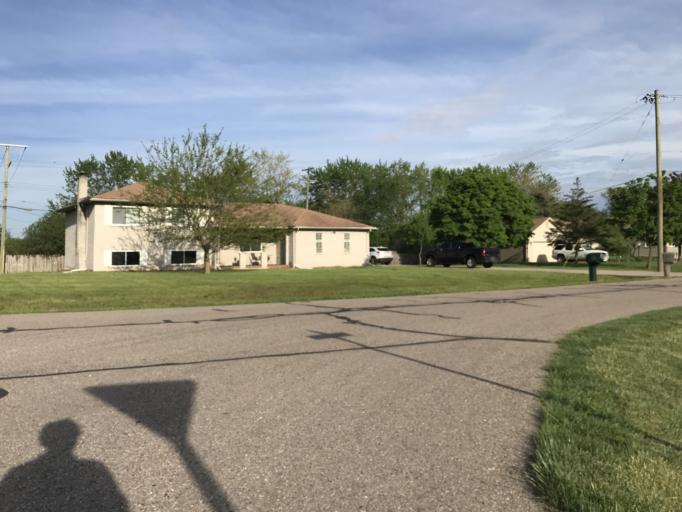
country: US
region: Michigan
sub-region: Oakland County
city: Farmington Hills
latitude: 42.4773
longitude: -83.3436
